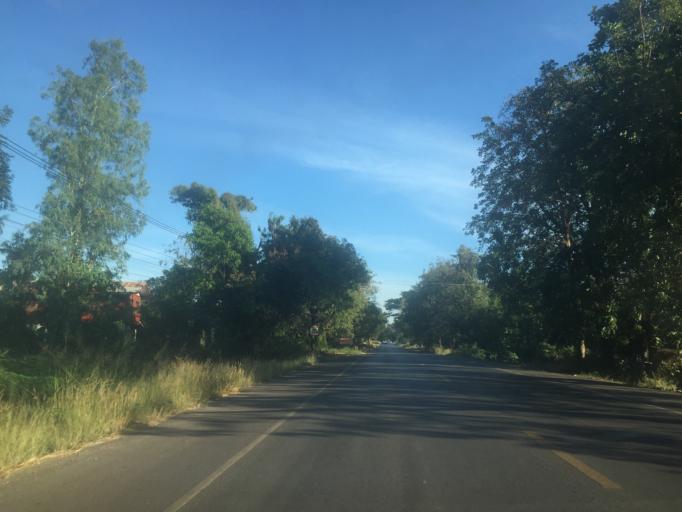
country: TH
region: Changwat Udon Thani
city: Si That
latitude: 16.9672
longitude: 103.2431
